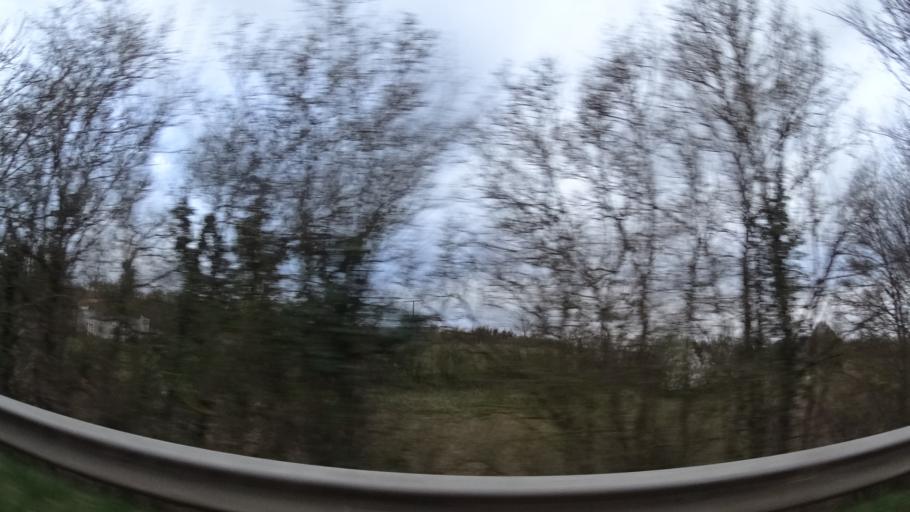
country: DE
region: Rheinland-Pfalz
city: Westhofen
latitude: 49.7015
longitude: 8.2402
